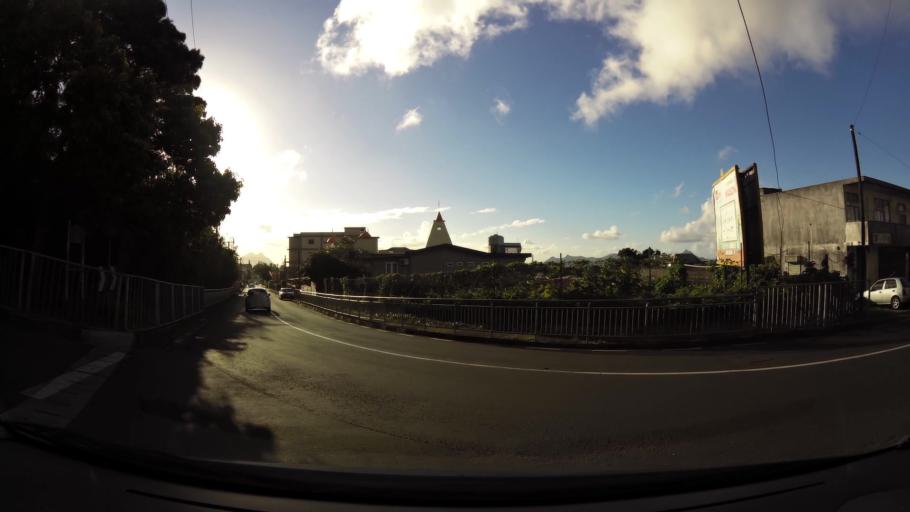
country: MU
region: Plaines Wilhems
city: Curepipe
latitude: -20.3133
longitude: 57.5156
